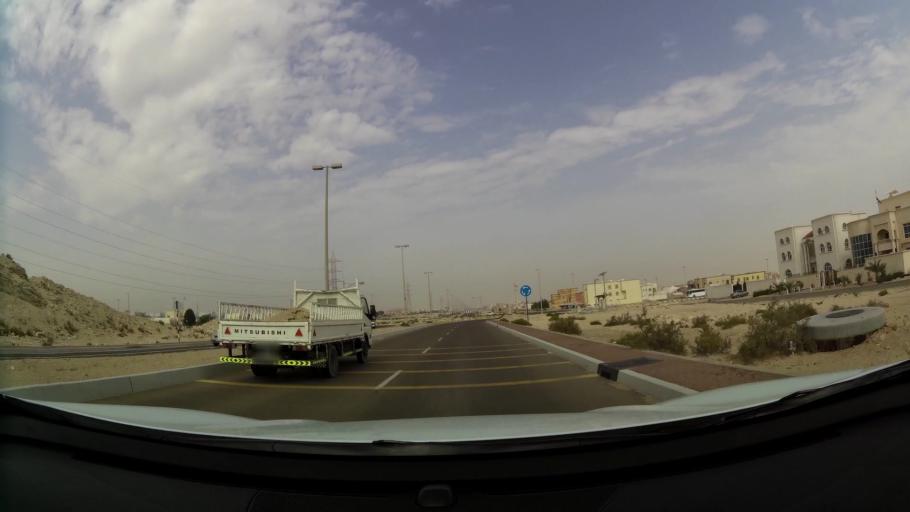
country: AE
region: Abu Dhabi
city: Abu Dhabi
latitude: 24.2997
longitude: 54.6574
